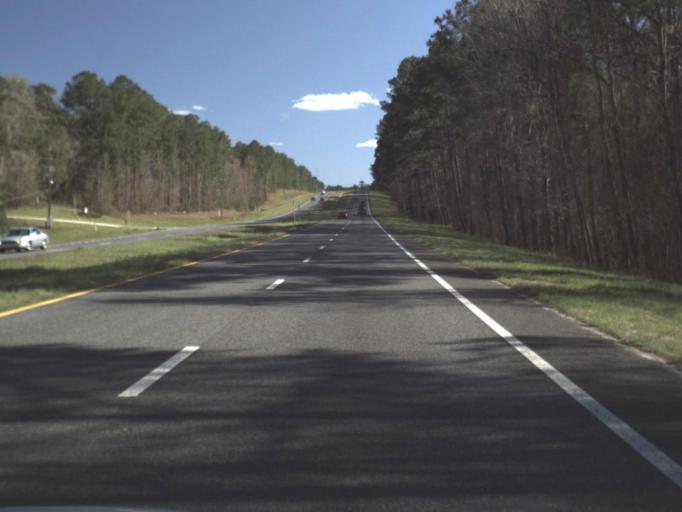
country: US
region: Florida
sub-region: Gadsden County
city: Midway
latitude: 30.5293
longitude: -84.4725
